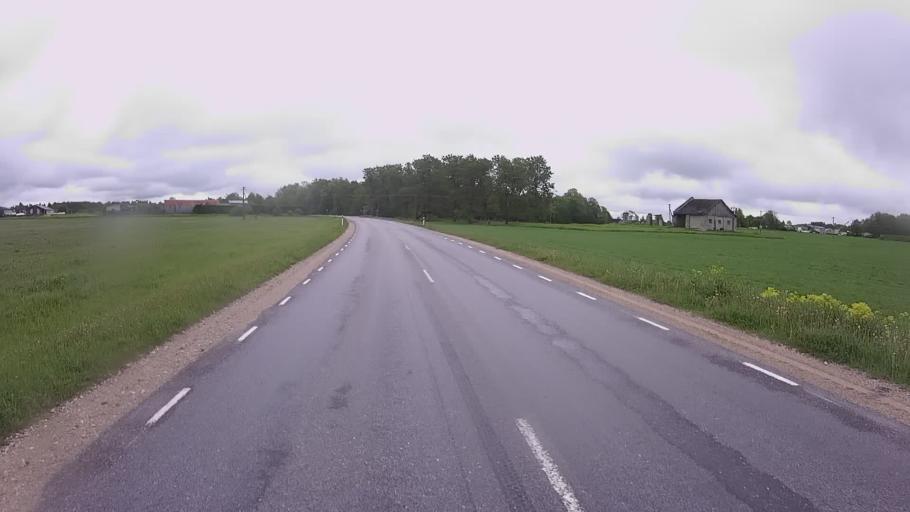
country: EE
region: Harju
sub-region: Nissi vald
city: Turba
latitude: 58.8961
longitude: 24.2315
